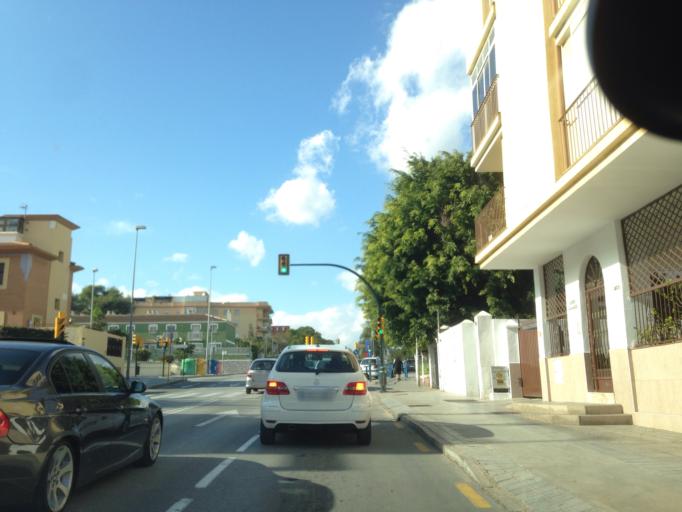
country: ES
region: Andalusia
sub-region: Provincia de Malaga
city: Malaga
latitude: 36.7237
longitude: -4.4543
